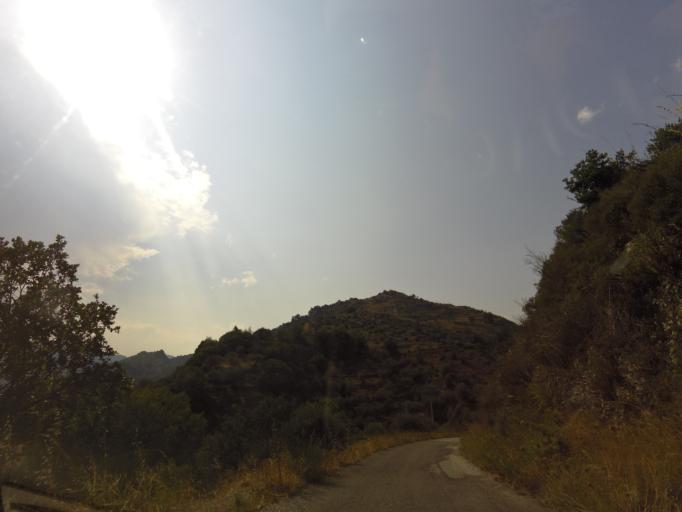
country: IT
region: Calabria
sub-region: Provincia di Reggio Calabria
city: Bivongi
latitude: 38.4927
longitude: 16.4639
